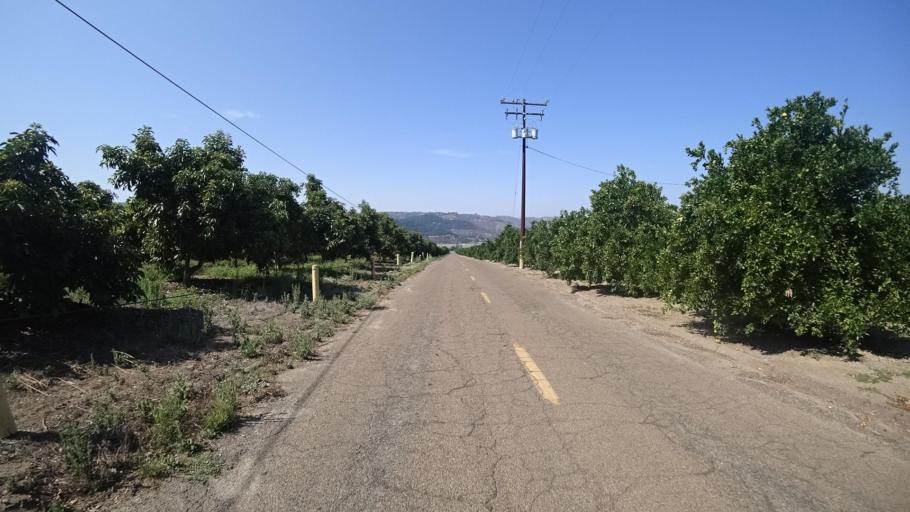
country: US
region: California
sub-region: San Diego County
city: Valley Center
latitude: 33.3189
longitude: -116.9847
